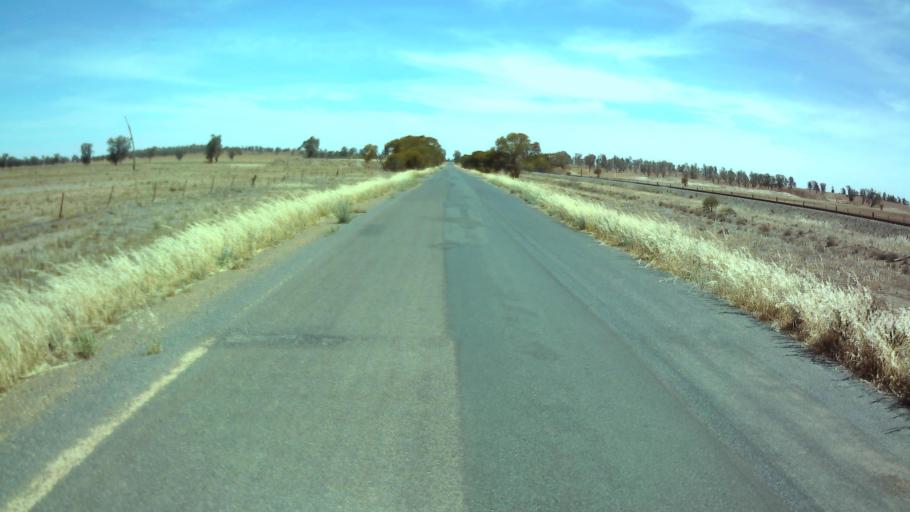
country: AU
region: New South Wales
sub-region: Weddin
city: Grenfell
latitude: -33.7623
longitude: 147.7605
